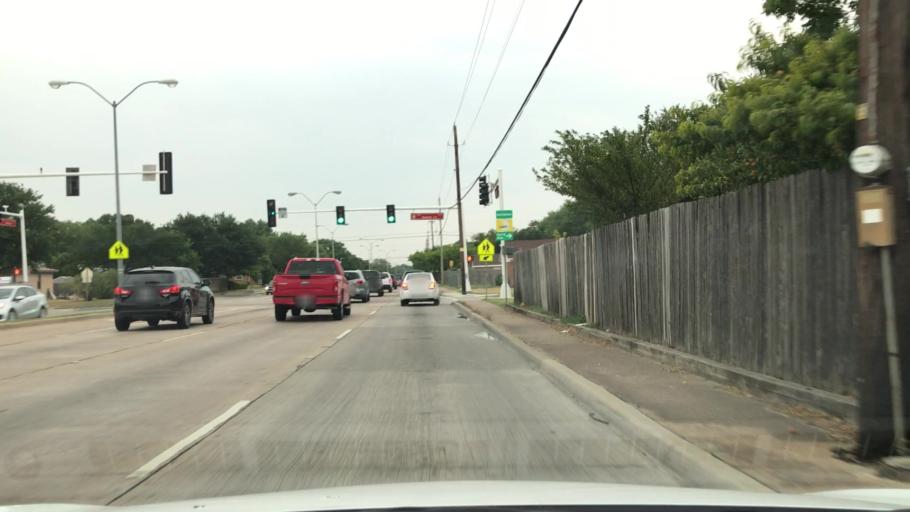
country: US
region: Texas
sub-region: Dallas County
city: Farmers Branch
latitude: 32.9339
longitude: -96.8886
